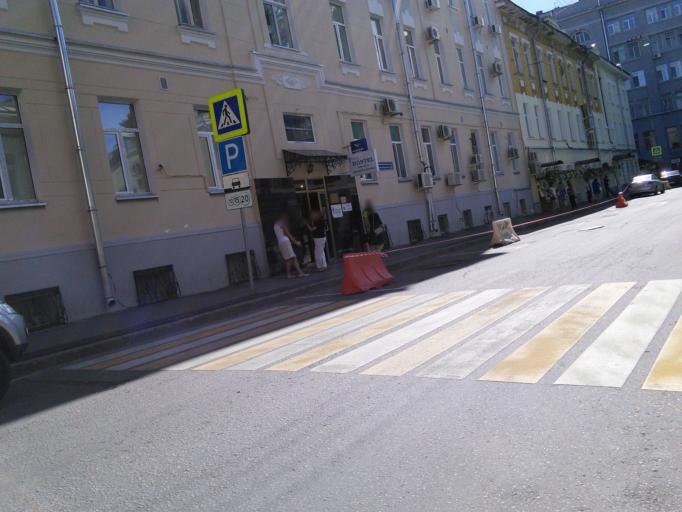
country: RU
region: Moscow
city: Moscow
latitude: 55.7586
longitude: 37.6343
